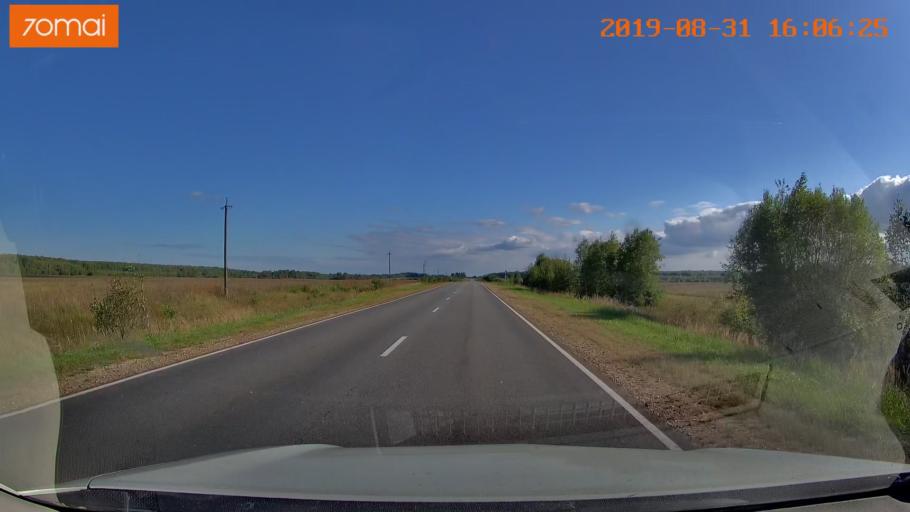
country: RU
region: Kaluga
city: Yukhnov
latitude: 54.6246
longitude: 35.3462
